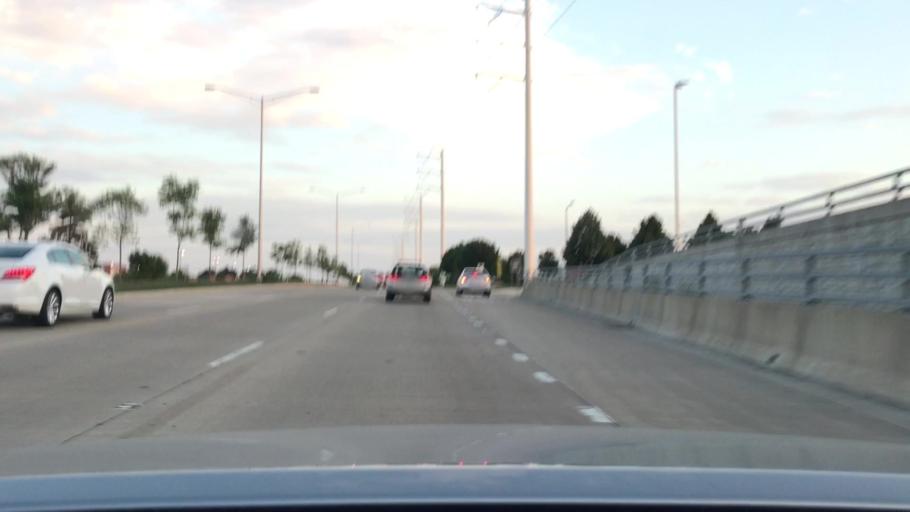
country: US
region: Illinois
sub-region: DuPage County
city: Warrenville
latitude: 41.7771
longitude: -88.2058
